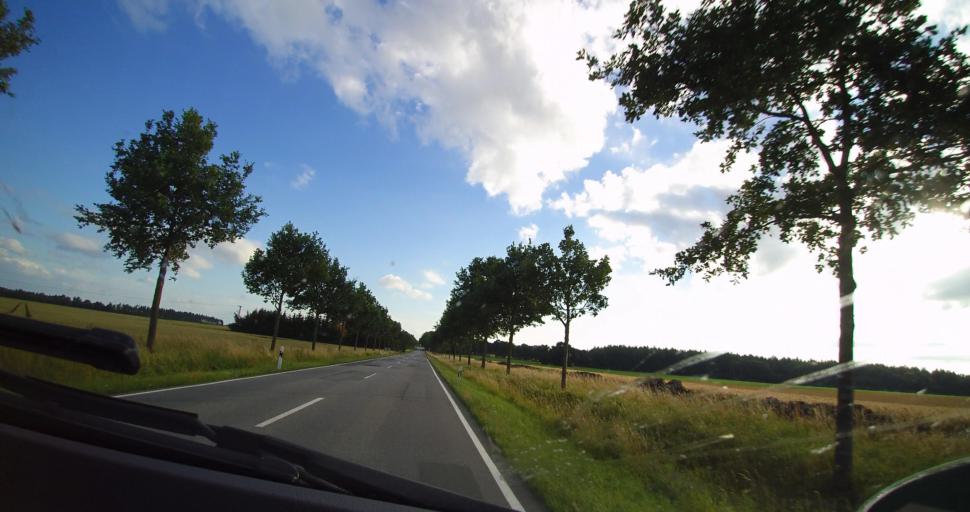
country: DE
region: Mecklenburg-Vorpommern
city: Franzburg
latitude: 54.1797
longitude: 12.8438
